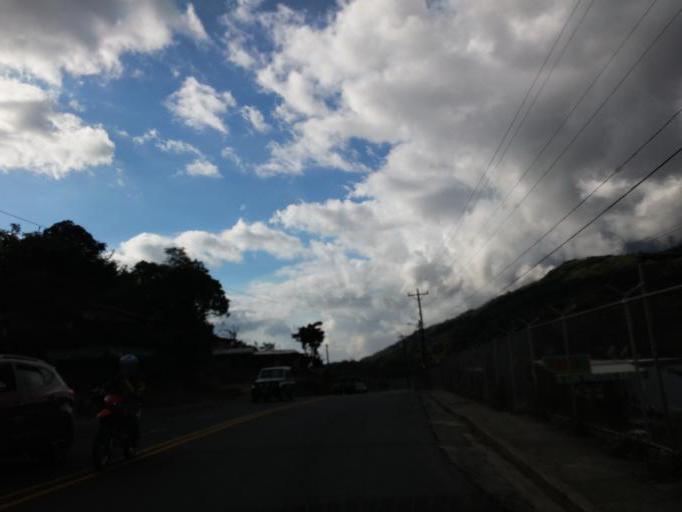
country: CR
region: San Jose
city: San Ignacio
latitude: 9.7969
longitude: -84.1324
